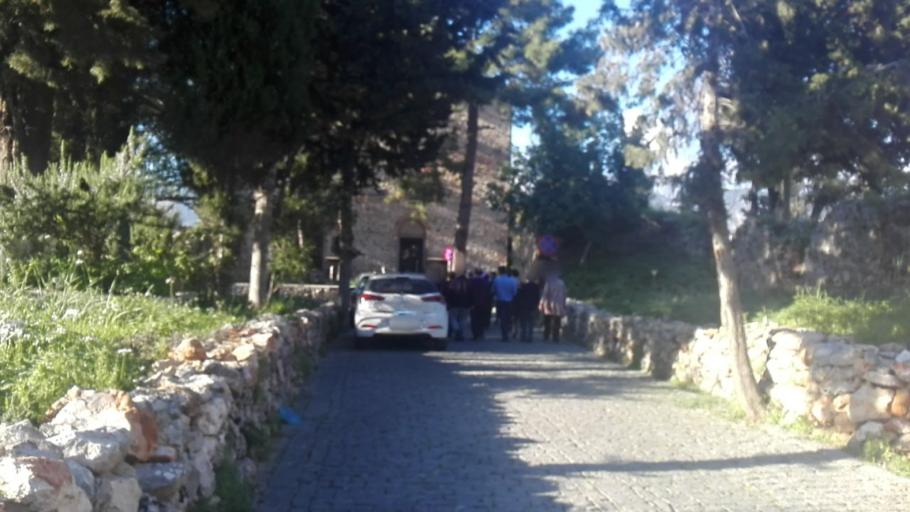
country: TR
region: Antalya
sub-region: Alanya
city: Alanya
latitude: 36.5345
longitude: 31.9930
